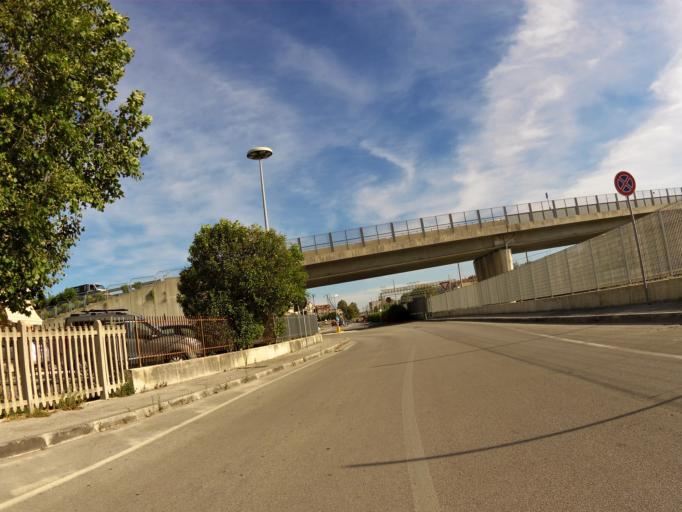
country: IT
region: The Marches
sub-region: Provincia di Macerata
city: Porto Recanati
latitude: 43.4320
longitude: 13.6623
